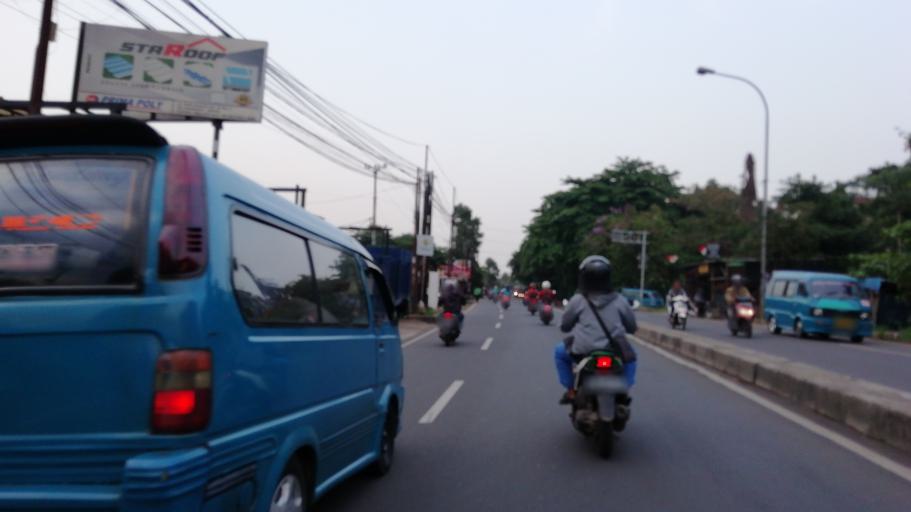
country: ID
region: West Java
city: Cibinong
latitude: -6.4330
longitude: 106.8552
